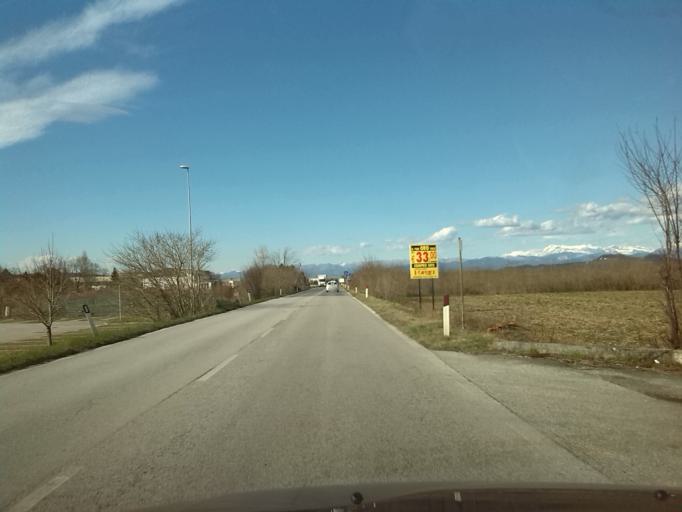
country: IT
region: Friuli Venezia Giulia
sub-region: Provincia di Gorizia
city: Mariano del Friuli
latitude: 45.8962
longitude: 13.4744
